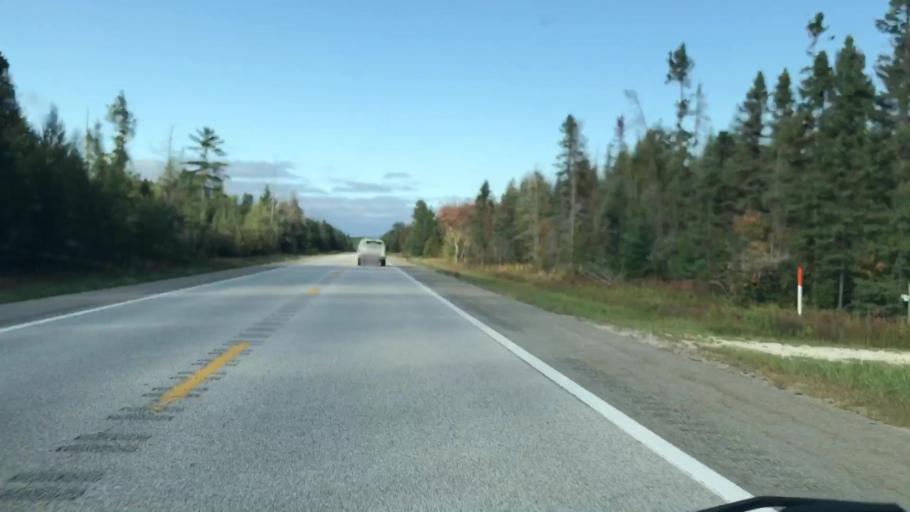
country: US
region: Michigan
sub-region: Luce County
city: Newberry
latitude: 46.3222
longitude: -85.1801
